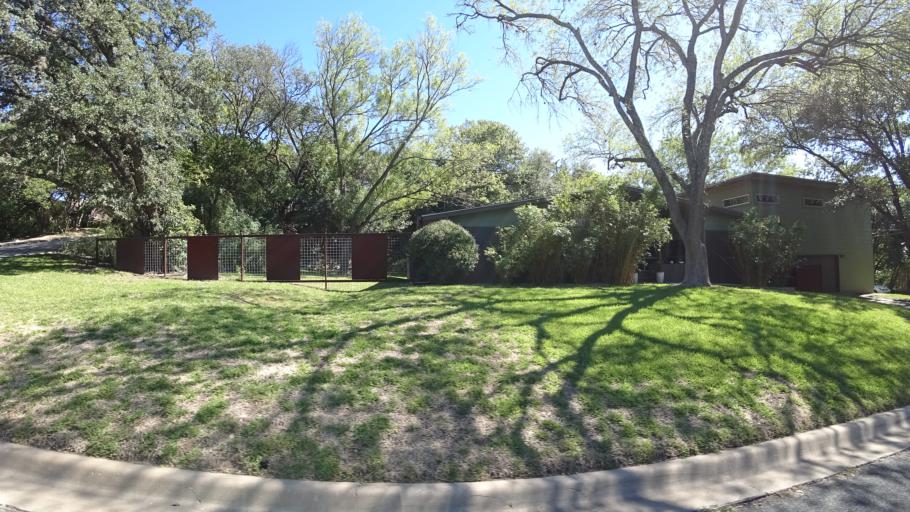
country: US
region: Texas
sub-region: Travis County
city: West Lake Hills
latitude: 30.3381
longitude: -97.7639
